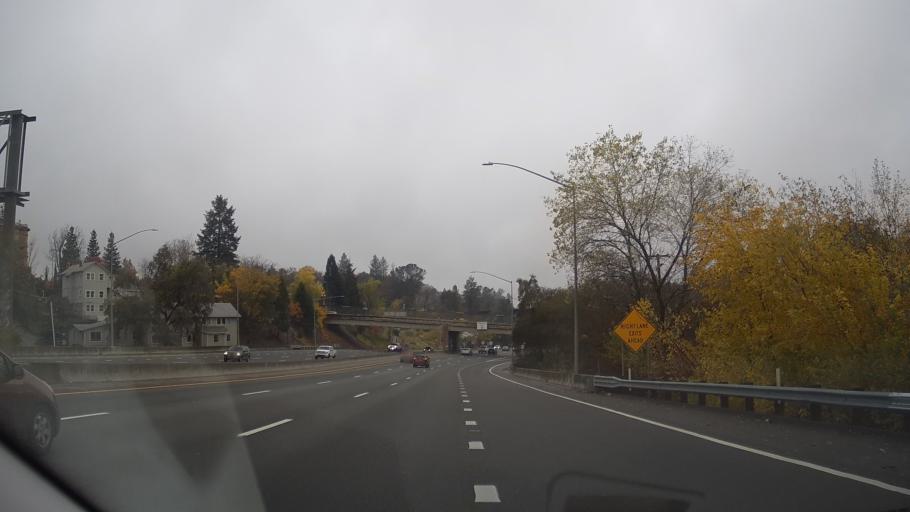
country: US
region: California
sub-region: Placer County
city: Auburn
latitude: 38.8989
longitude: -121.0773
